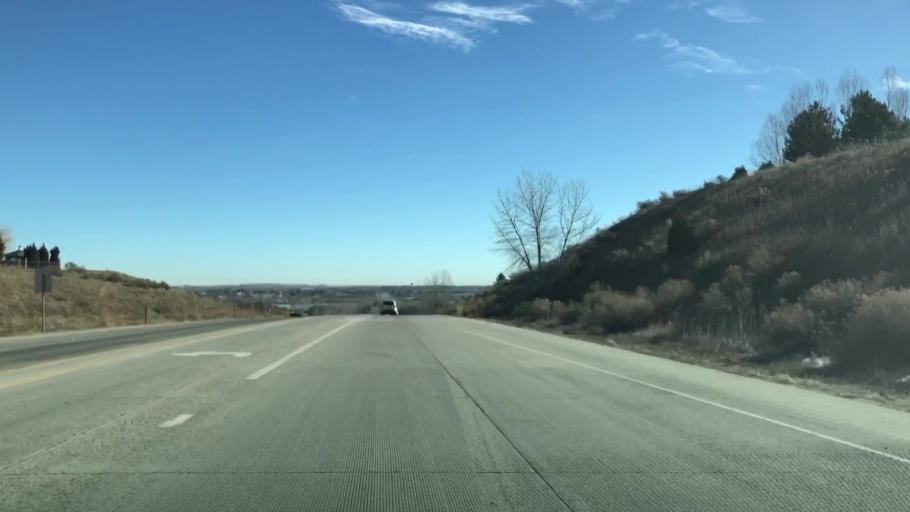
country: US
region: Colorado
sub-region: Weld County
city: Windsor
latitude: 40.4793
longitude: -104.9656
